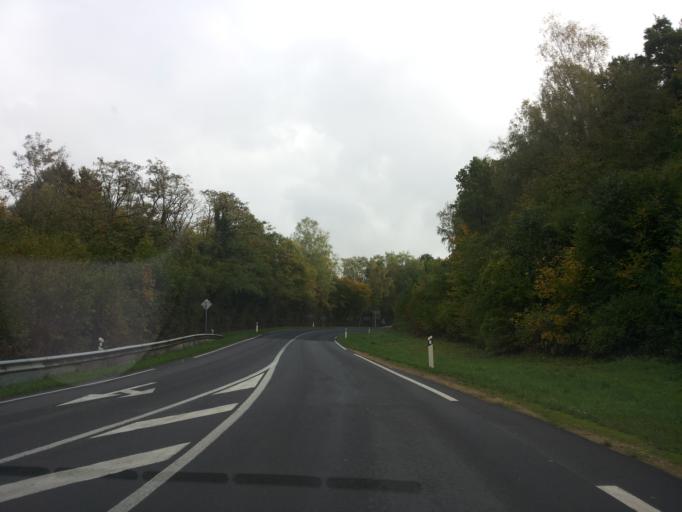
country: FR
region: Lorraine
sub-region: Departement de la Meuse
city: Montmedy
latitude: 49.4658
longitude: 5.3993
